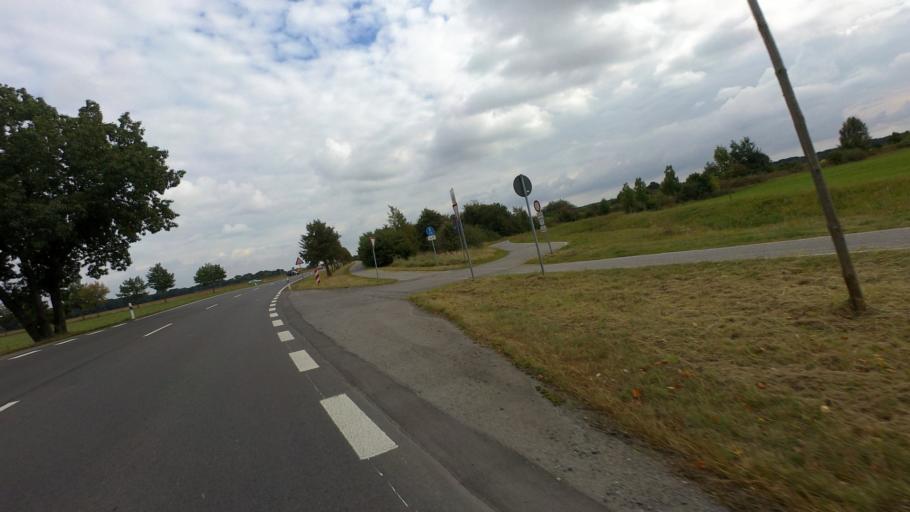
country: DE
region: Saxony
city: Hoyerswerda
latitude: 51.4568
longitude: 14.2051
